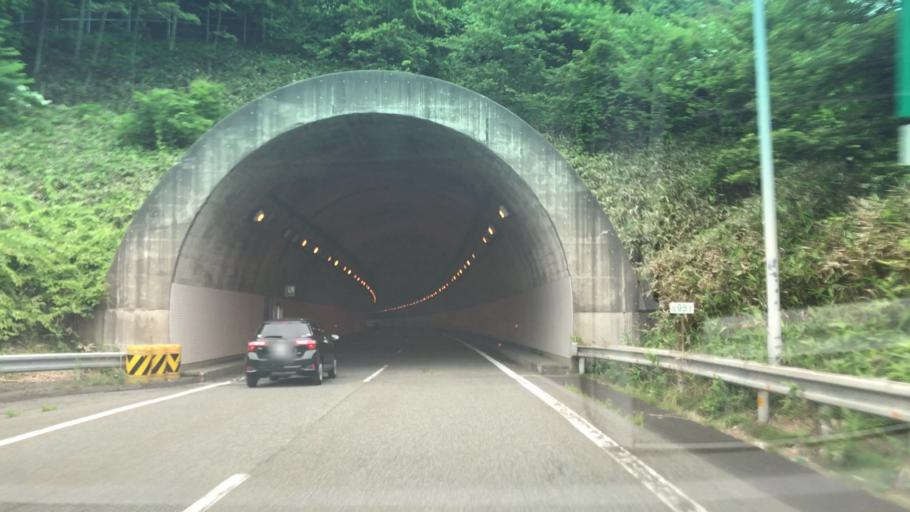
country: JP
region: Hokkaido
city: Shiraoi
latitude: 42.4724
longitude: 141.2133
